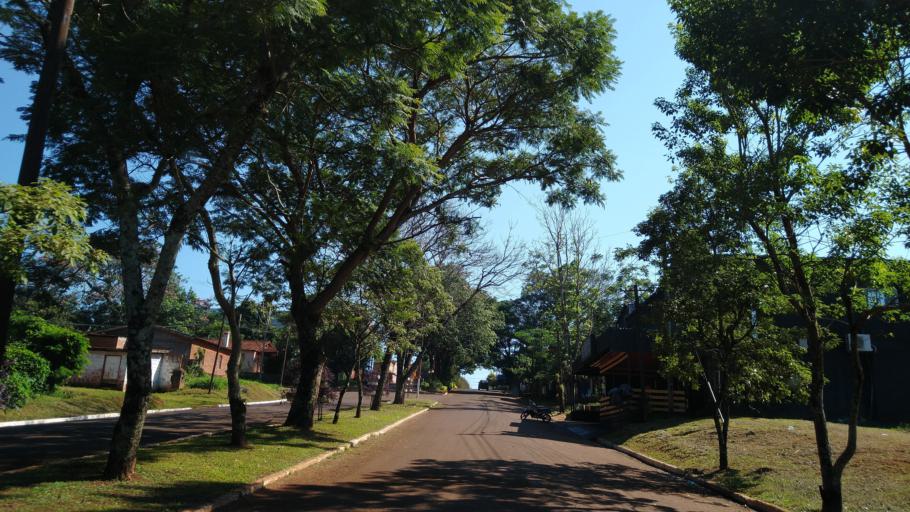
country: AR
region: Misiones
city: Puerto Esperanza
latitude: -26.0270
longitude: -54.6123
